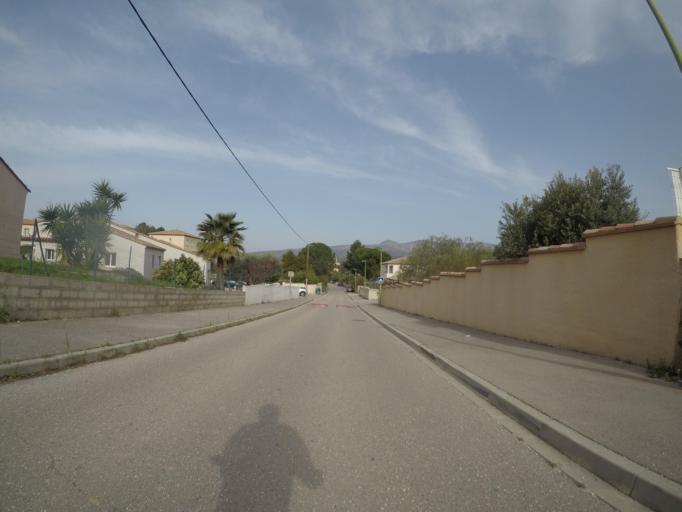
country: FR
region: Languedoc-Roussillon
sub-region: Departement des Pyrenees-Orientales
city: Baixas
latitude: 42.7758
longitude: 2.7930
